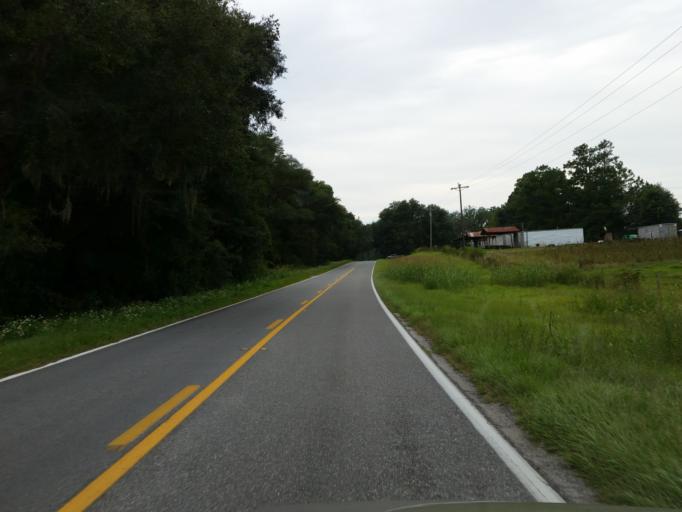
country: US
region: Florida
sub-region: Alachua County
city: High Springs
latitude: 29.9505
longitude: -82.5330
